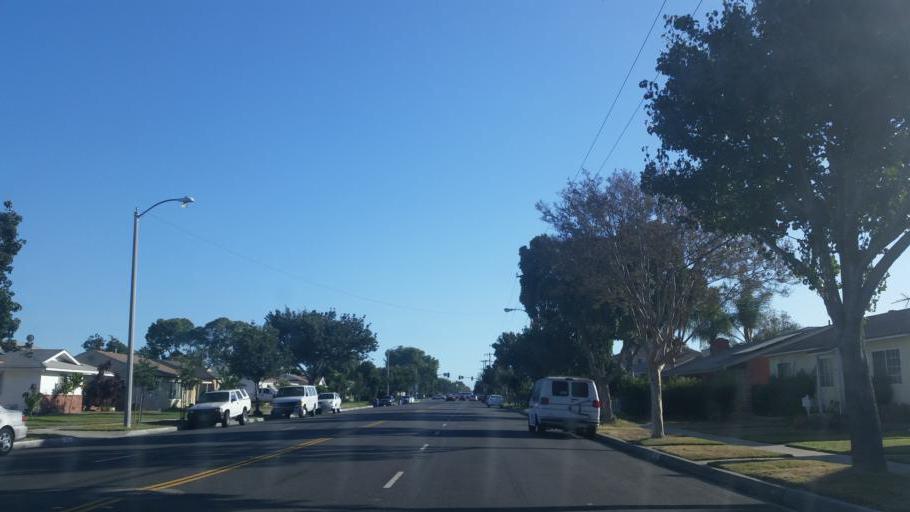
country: US
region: California
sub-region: Los Angeles County
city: Lakewood
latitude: 33.8625
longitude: -118.1339
